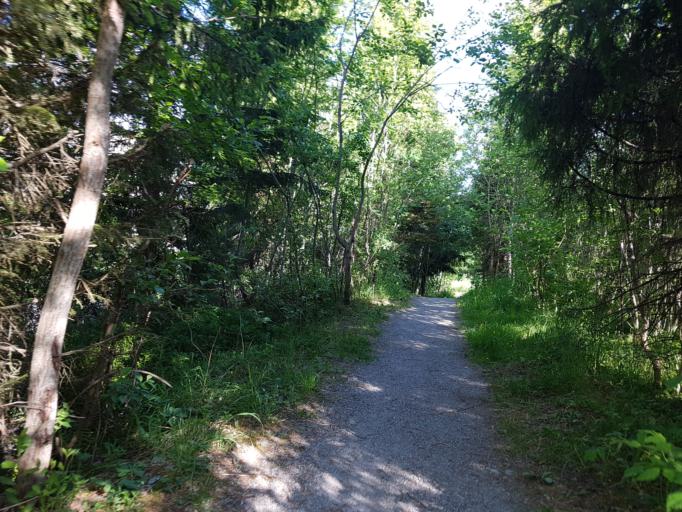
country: NO
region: Sor-Trondelag
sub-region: Trondheim
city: Trondheim
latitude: 63.3970
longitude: 10.3242
